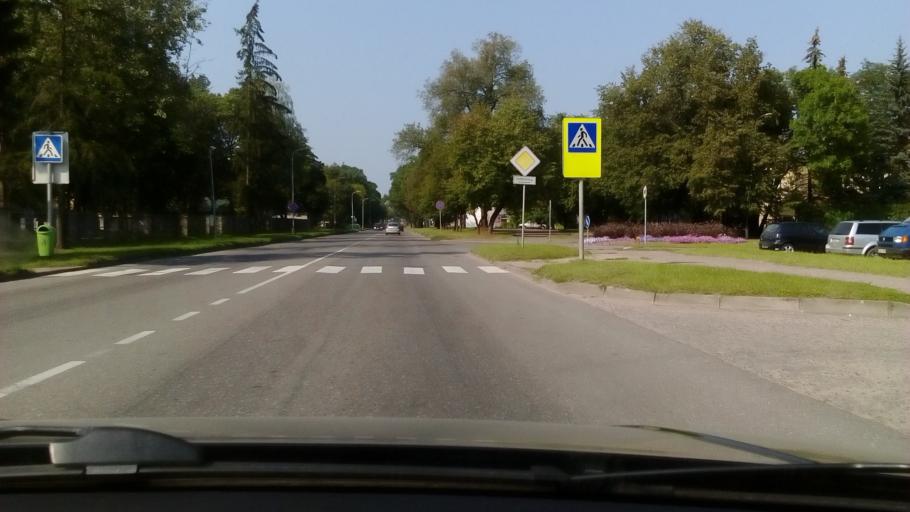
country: LT
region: Alytaus apskritis
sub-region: Alytus
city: Alytus
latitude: 54.3824
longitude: 24.0552
